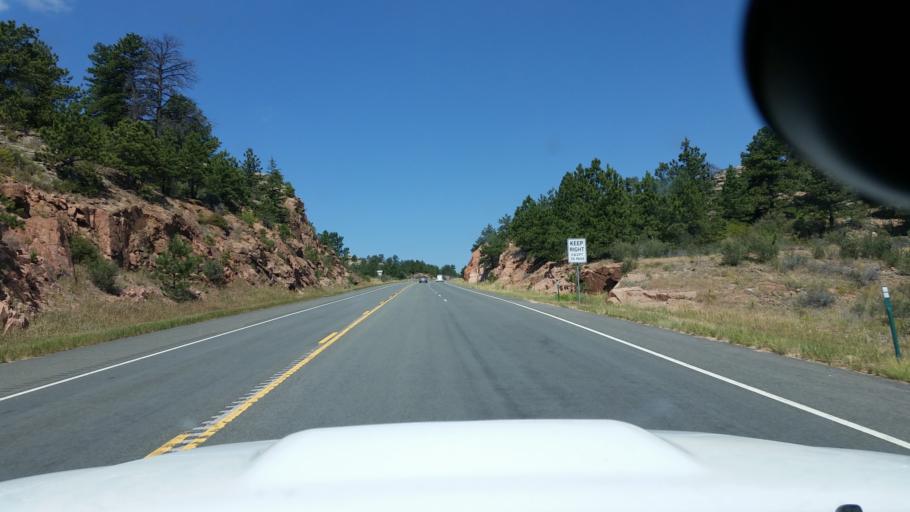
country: US
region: Colorado
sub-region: Larimer County
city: Laporte
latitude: 40.9628
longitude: -105.3689
